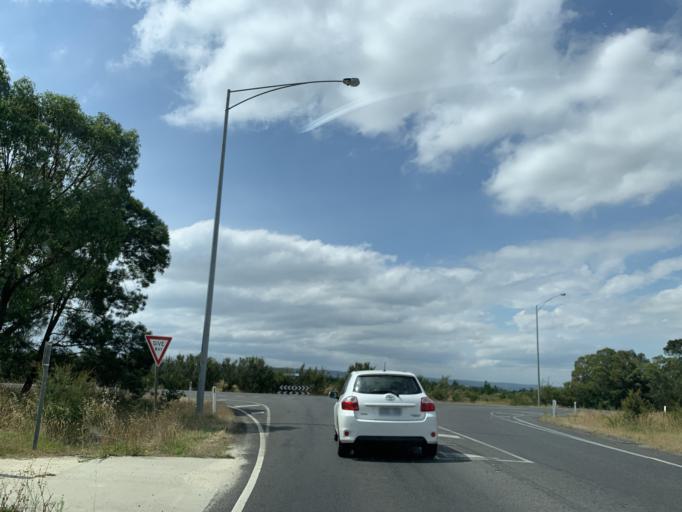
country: AU
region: Victoria
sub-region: Latrobe
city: Traralgon
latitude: -38.2013
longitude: 146.4790
